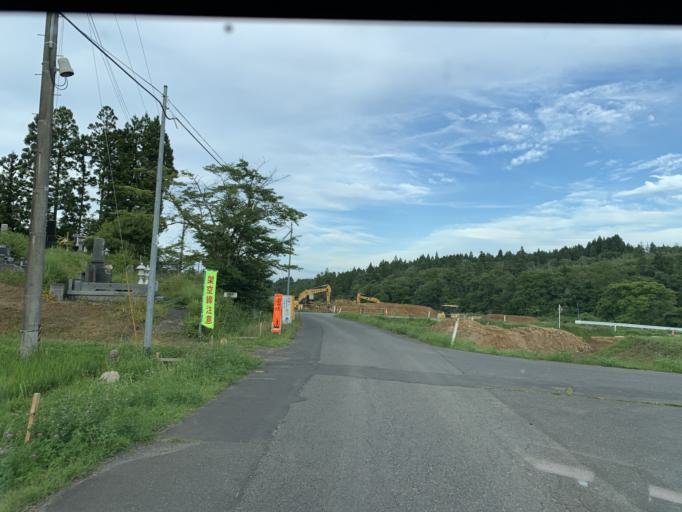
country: JP
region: Iwate
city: Ichinoseki
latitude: 38.9126
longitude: 141.0143
